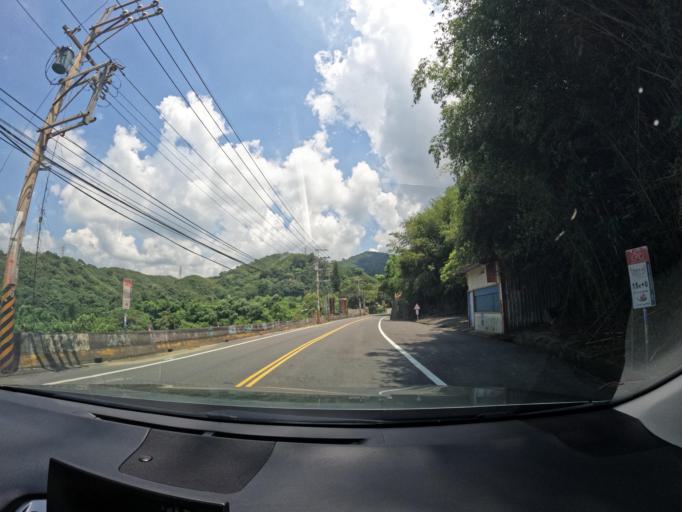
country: TW
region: Taiwan
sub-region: Miaoli
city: Miaoli
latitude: 24.4025
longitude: 120.7936
